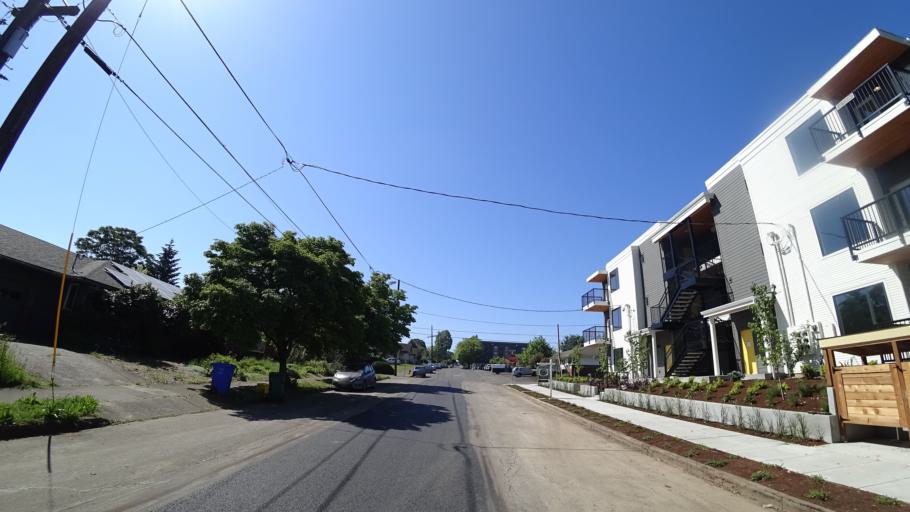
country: US
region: Oregon
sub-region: Multnomah County
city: Portland
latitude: 45.5736
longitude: -122.6604
